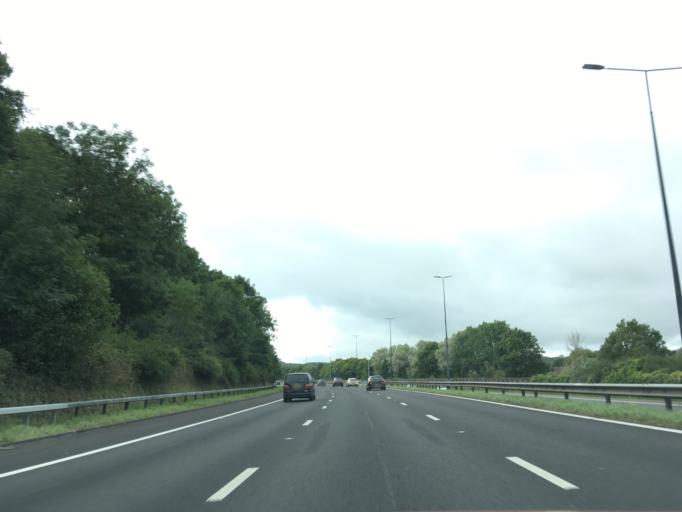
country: GB
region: Wales
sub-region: Newport
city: Langstone
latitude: 51.6023
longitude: -2.9000
